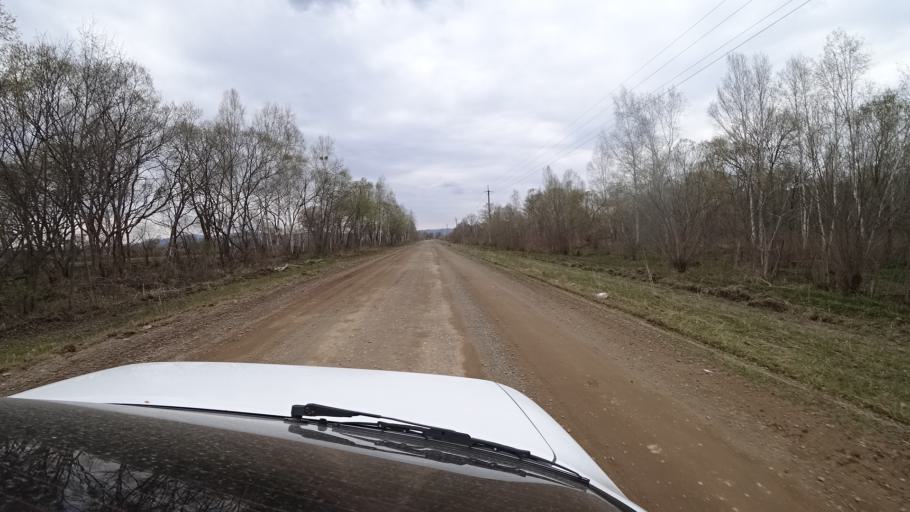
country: RU
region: Primorskiy
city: Novopokrovka
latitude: 45.5601
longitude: 134.3432
